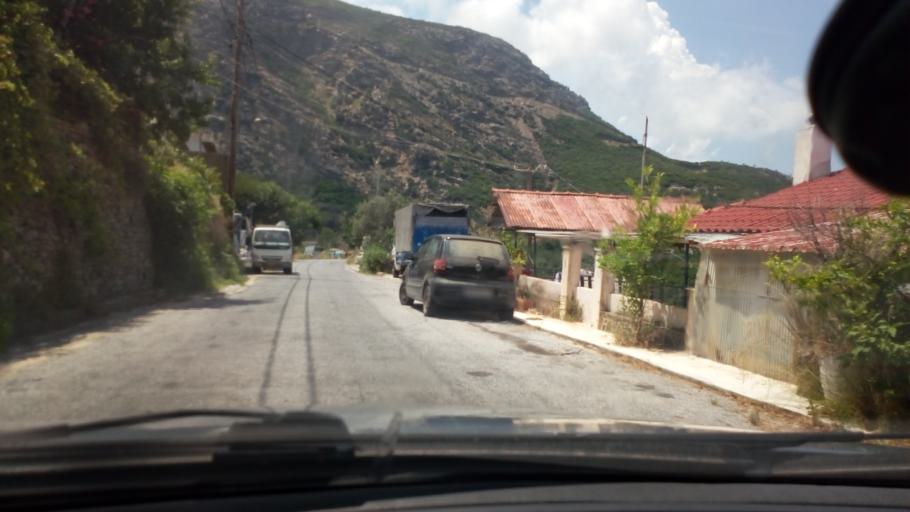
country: GR
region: North Aegean
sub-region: Nomos Samou
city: Agios Kirykos
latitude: 37.6409
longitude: 26.2602
